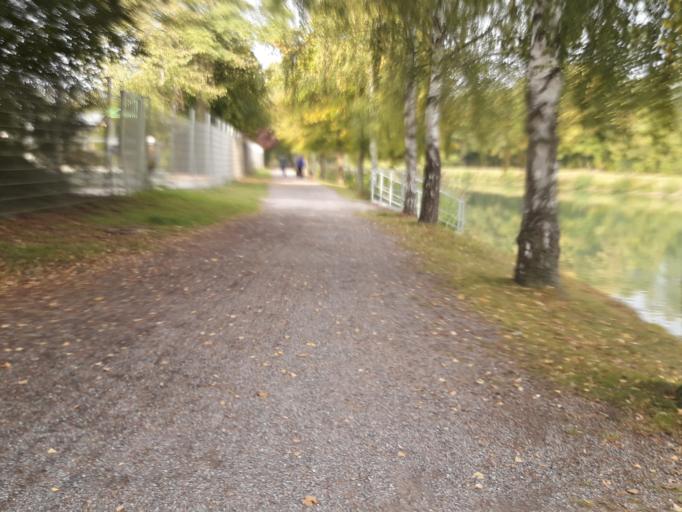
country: DE
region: North Rhine-Westphalia
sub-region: Regierungsbezirk Munster
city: Muenster
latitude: 51.8967
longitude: 7.6549
